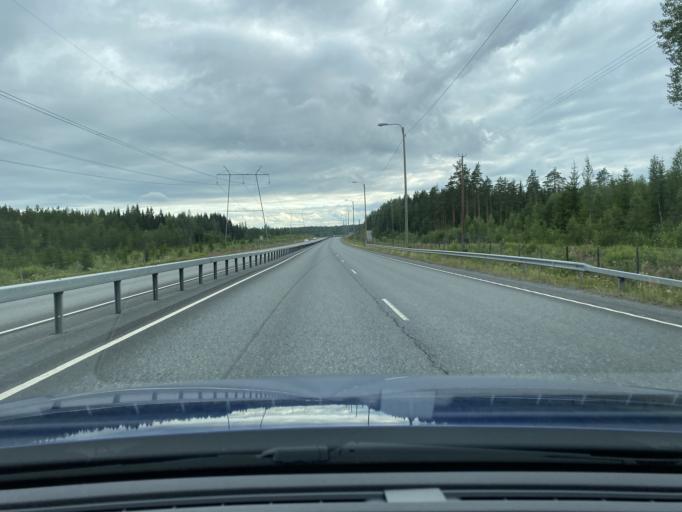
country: FI
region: Pirkanmaa
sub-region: Tampere
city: Kangasala
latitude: 61.6095
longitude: 24.1445
